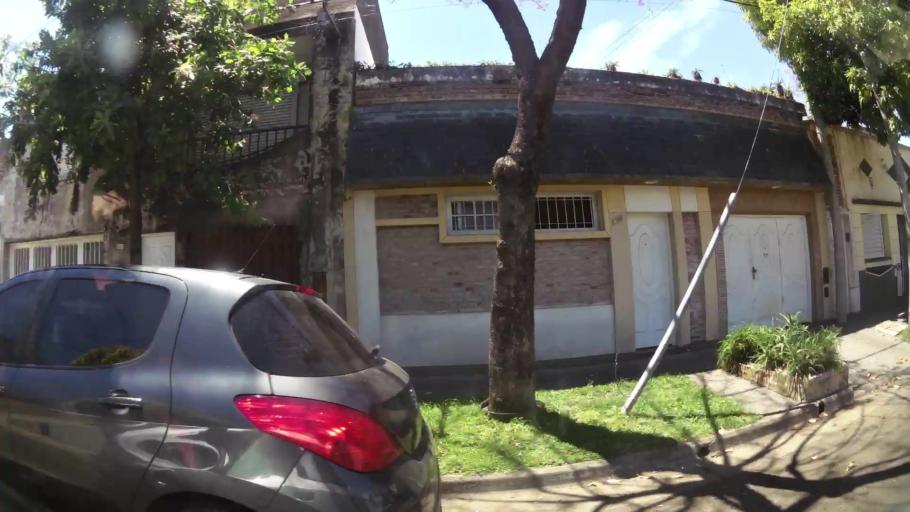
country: AR
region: Santa Fe
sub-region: Departamento de Rosario
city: Rosario
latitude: -32.9449
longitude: -60.7048
